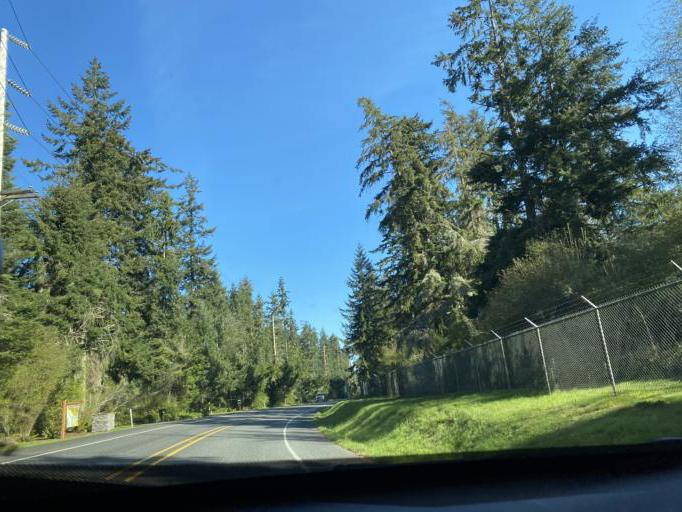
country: US
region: Washington
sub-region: Island County
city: Freeland
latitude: 48.0714
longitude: -122.6046
